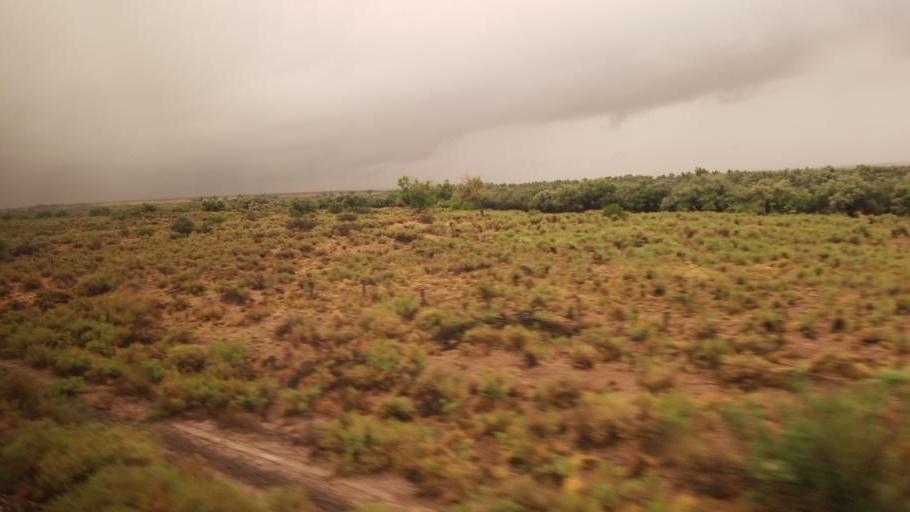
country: US
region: Arizona
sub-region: Navajo County
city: Joseph City
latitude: 34.9664
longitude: -110.4240
